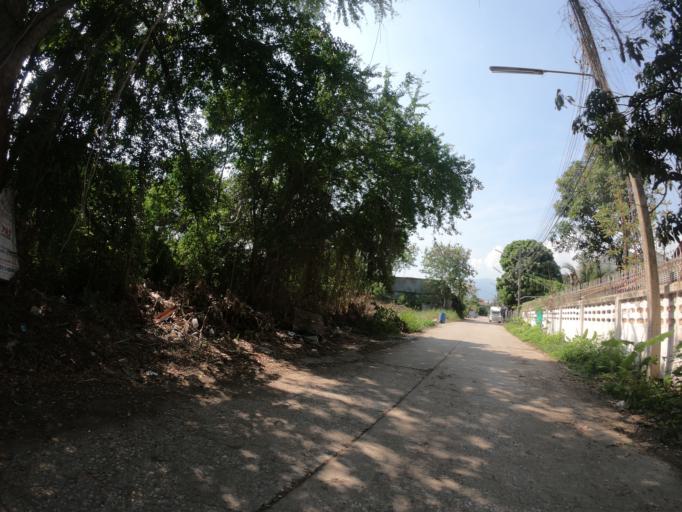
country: TH
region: Chiang Mai
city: Chiang Mai
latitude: 18.8079
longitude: 99.0007
